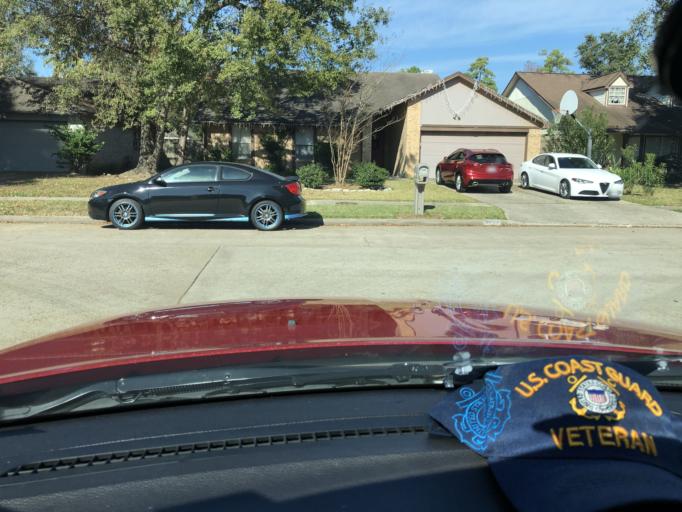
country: US
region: Texas
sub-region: Harris County
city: Tomball
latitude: 30.0211
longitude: -95.5574
